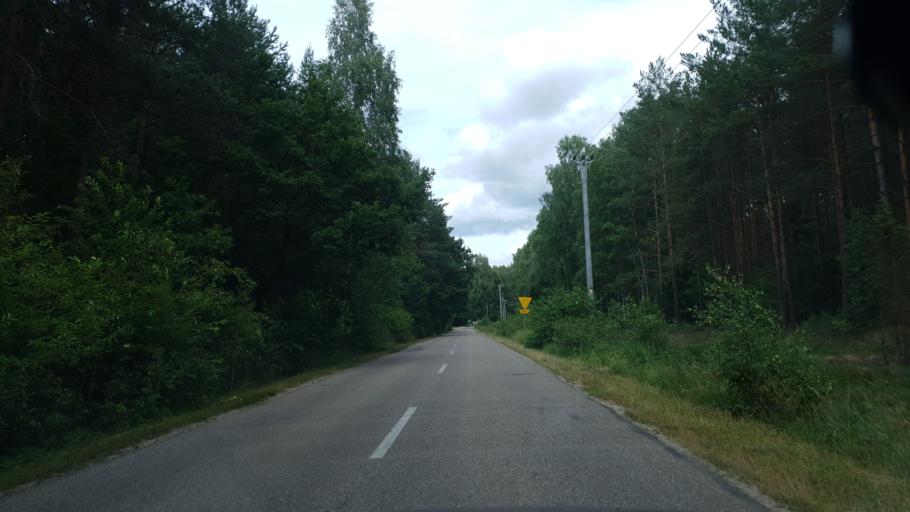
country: PL
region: Pomeranian Voivodeship
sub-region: Powiat kartuski
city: Stezyca
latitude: 54.2551
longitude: 18.0167
